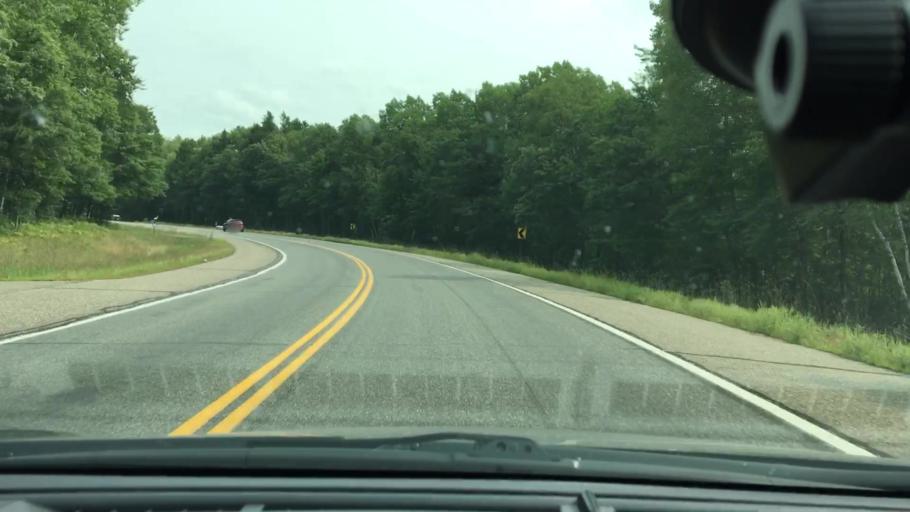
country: US
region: Minnesota
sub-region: Crow Wing County
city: Breezy Point
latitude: 46.5302
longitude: -94.1964
